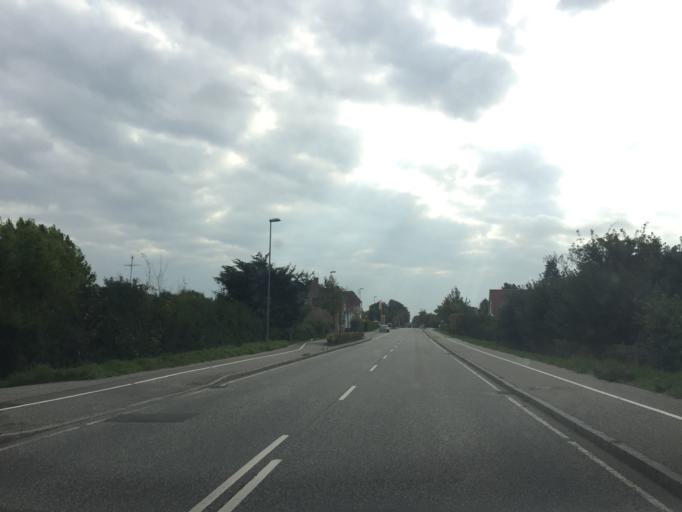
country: DK
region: Zealand
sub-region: Vordingborg Kommune
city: Praesto
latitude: 55.1661
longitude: 11.9807
